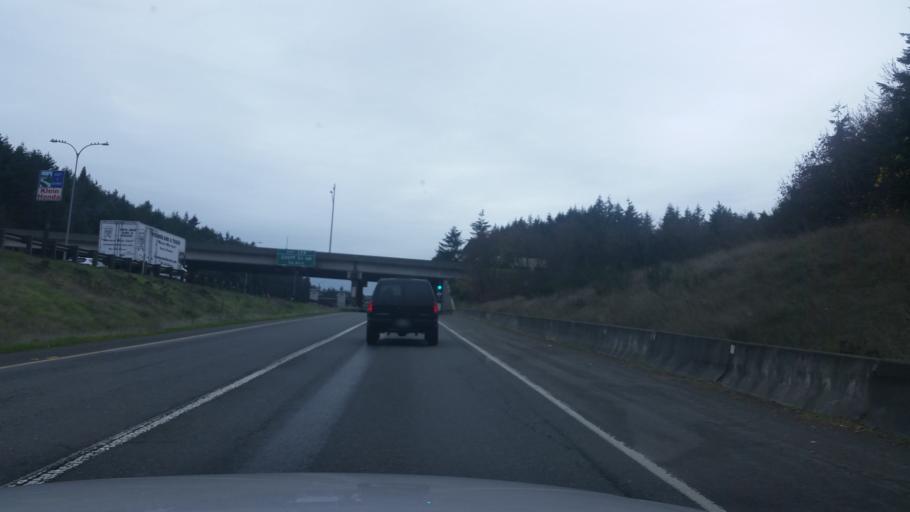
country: US
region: Washington
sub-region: Snohomish County
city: Mountlake Terrace
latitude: 47.7837
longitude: -122.3159
